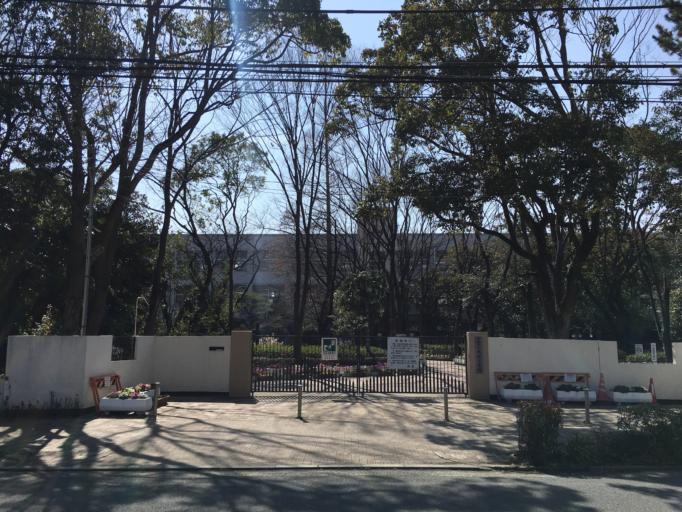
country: JP
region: Hyogo
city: Amagasaki
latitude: 34.7210
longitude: 135.3984
